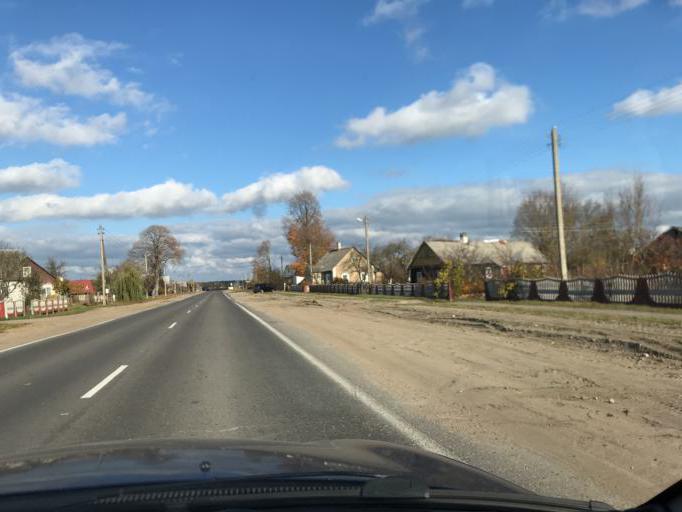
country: LT
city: Salcininkai
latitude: 54.2546
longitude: 25.3568
